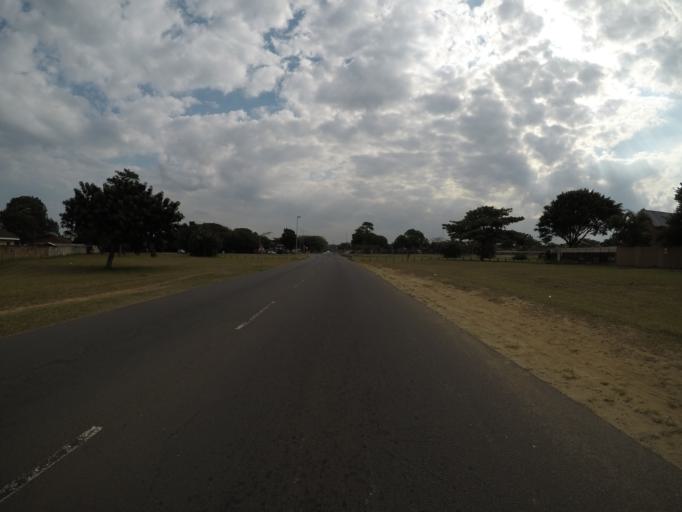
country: ZA
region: KwaZulu-Natal
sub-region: uThungulu District Municipality
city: Richards Bay
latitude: -28.7405
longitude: 32.0786
